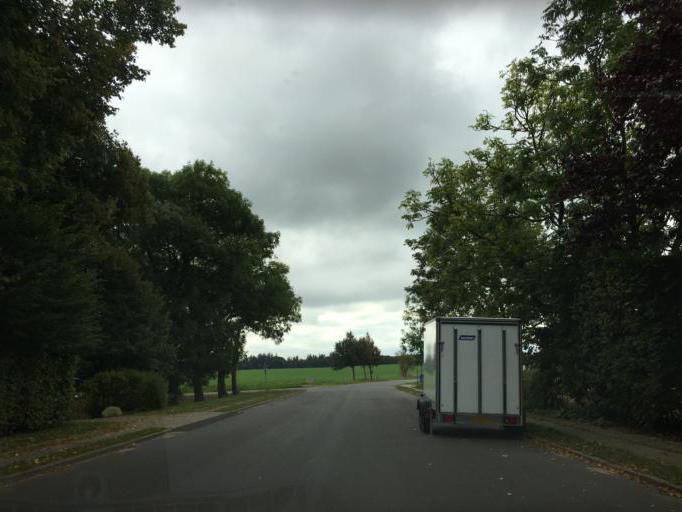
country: DK
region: South Denmark
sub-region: Kolding Kommune
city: Kolding
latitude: 55.5817
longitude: 9.4925
